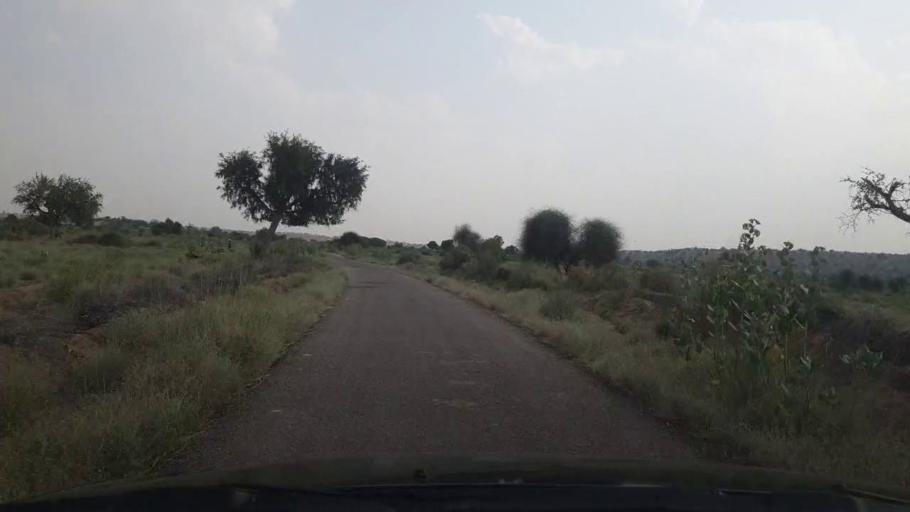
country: PK
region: Sindh
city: Islamkot
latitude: 25.0108
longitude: 70.5957
